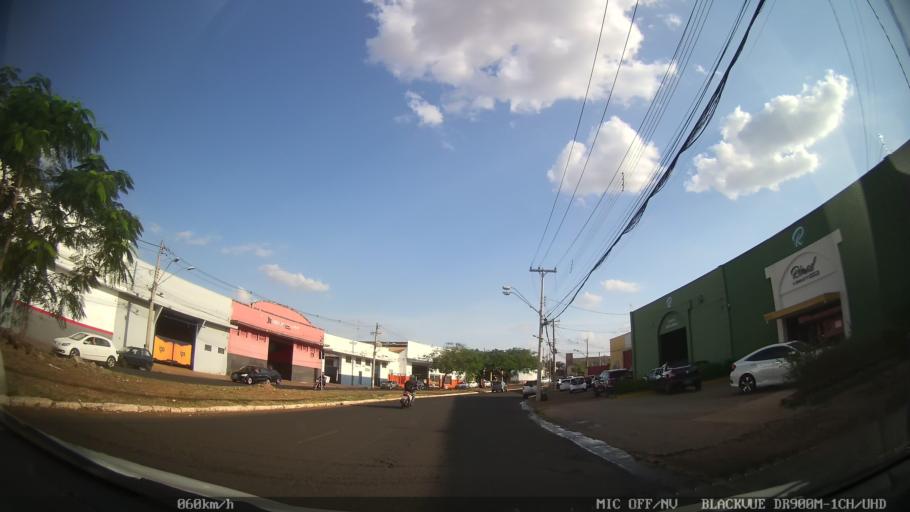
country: BR
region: Sao Paulo
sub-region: Ribeirao Preto
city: Ribeirao Preto
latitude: -21.1470
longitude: -47.8003
